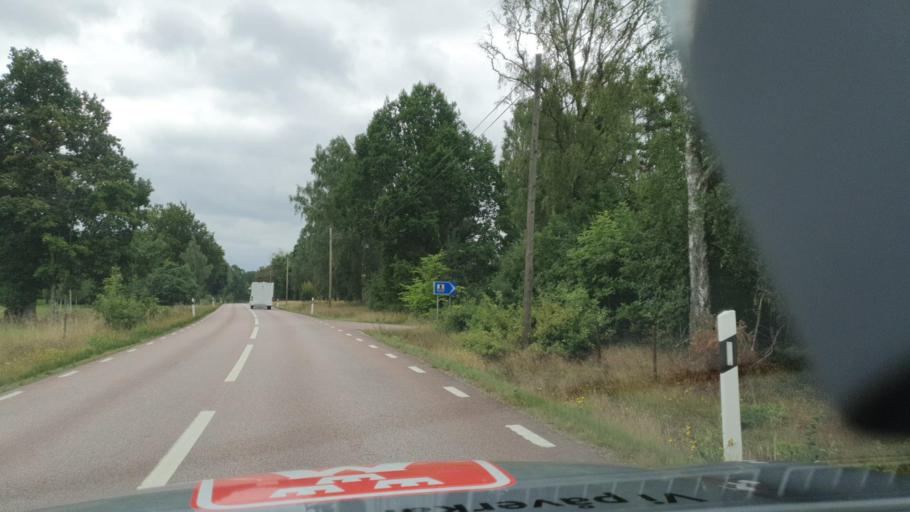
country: SE
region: Kalmar
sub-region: Emmaboda Kommun
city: Emmaboda
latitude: 56.4689
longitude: 15.5942
